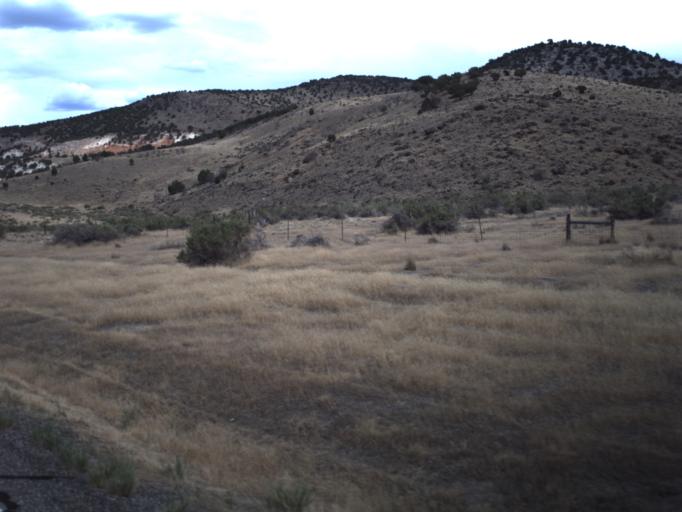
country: US
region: Utah
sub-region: Sevier County
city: Richfield
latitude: 38.7728
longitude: -111.9593
